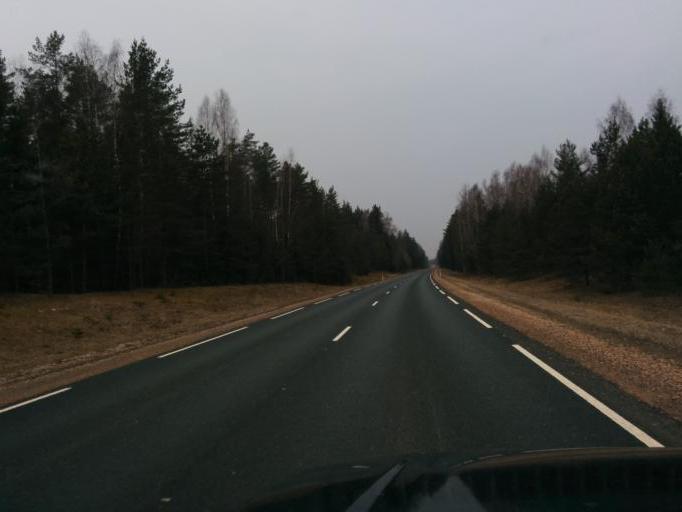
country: LV
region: Ikskile
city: Ikskile
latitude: 56.8038
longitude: 24.5010
